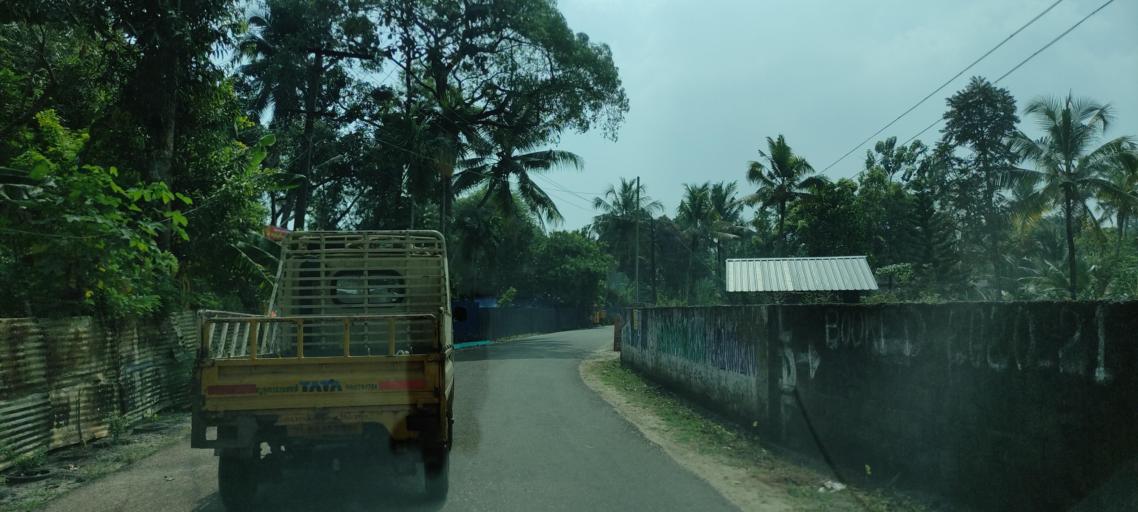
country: IN
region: Kerala
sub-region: Alappuzha
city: Shertallai
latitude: 9.6097
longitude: 76.3470
